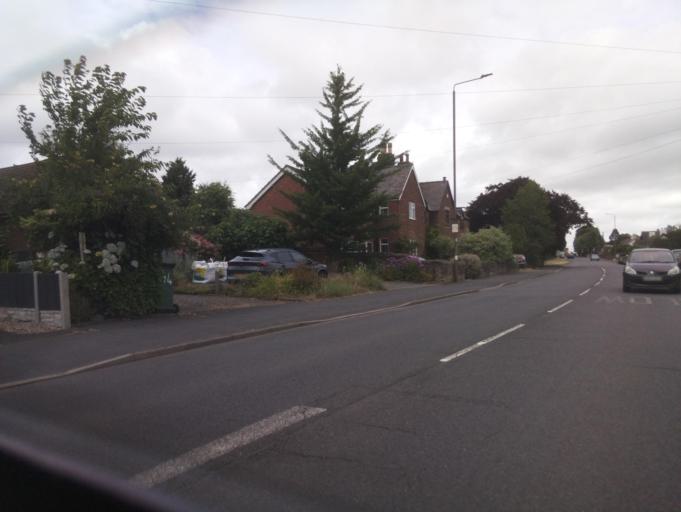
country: GB
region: England
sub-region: Derbyshire
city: Ripley
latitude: 52.9946
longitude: -1.3943
